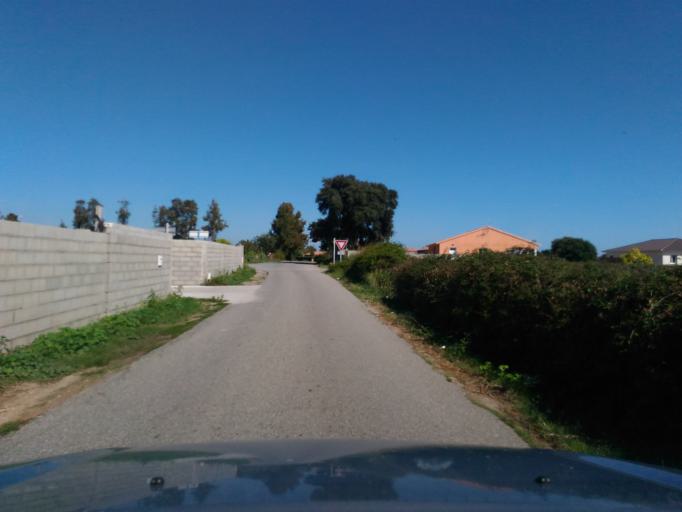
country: FR
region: Corsica
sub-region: Departement de la Haute-Corse
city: Aleria
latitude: 42.1102
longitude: 9.4794
